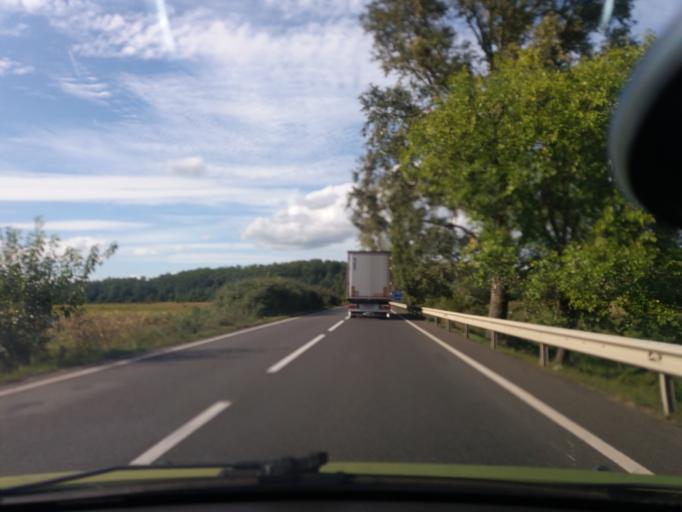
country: RO
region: Arad
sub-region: Comuna Varadia de Mures
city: Varadia de Mures
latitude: 46.0199
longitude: 22.1481
